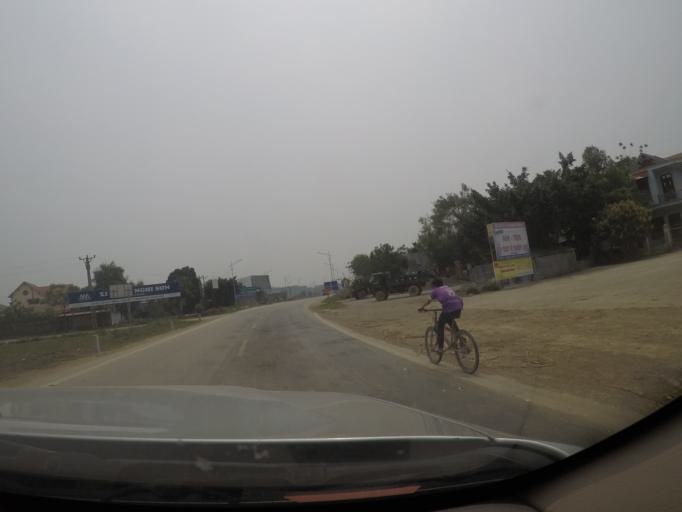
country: VN
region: Thanh Hoa
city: Thi Tran Thuong Xuan
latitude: 19.9111
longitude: 105.3977
